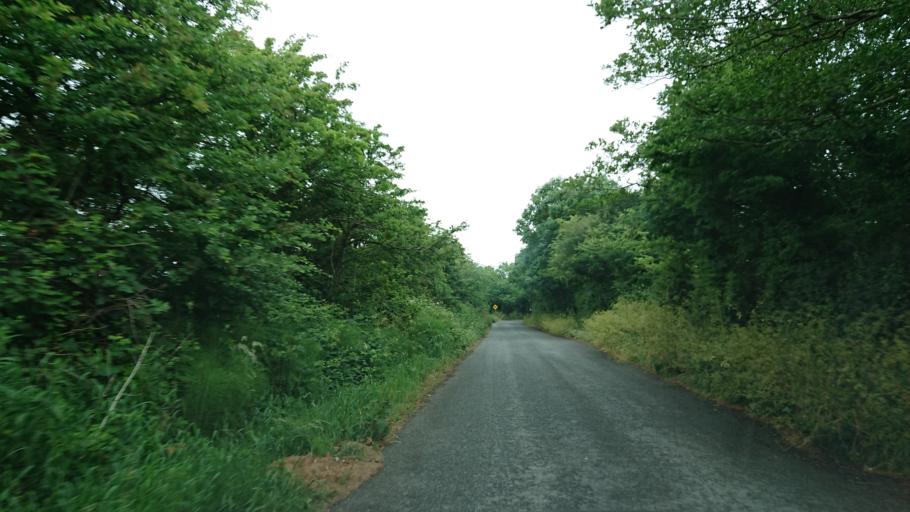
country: IE
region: Munster
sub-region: Waterford
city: Waterford
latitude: 52.2257
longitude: -7.1469
